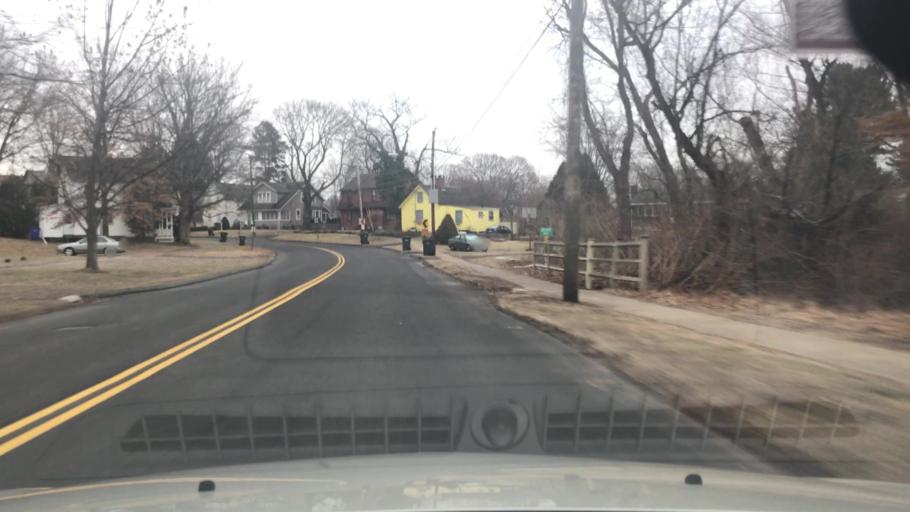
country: US
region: Connecticut
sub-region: Hartford County
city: Wethersfield
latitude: 41.7060
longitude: -72.6587
